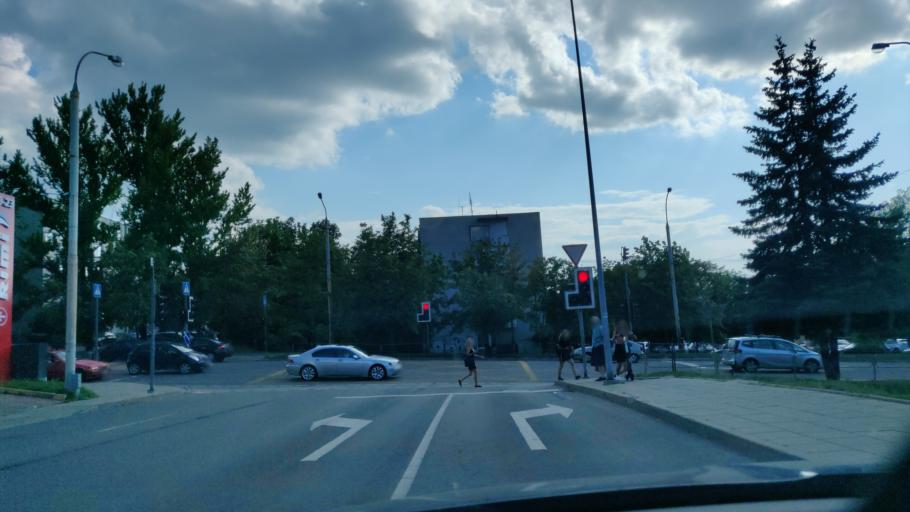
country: LT
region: Vilnius County
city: Vilkpede
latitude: 54.6739
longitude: 25.2546
